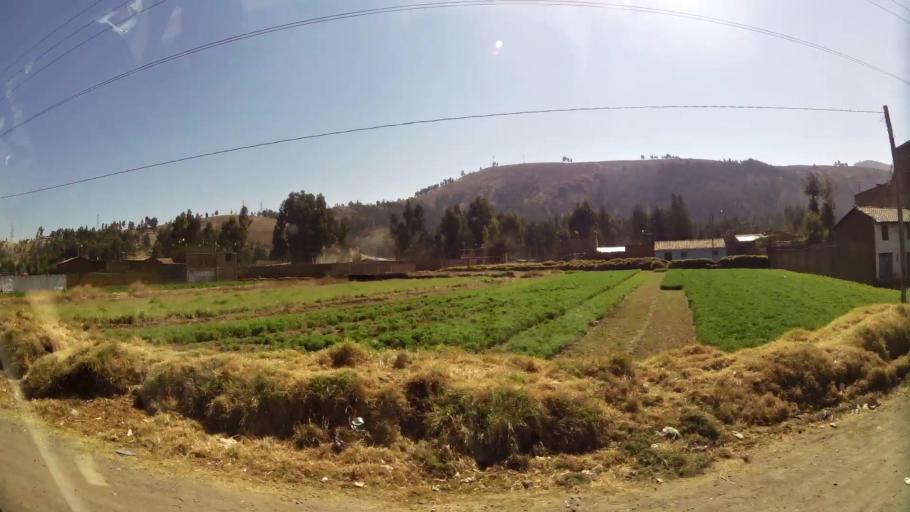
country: PE
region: Junin
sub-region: Provincia de Concepcion
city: Concepcion
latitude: -11.9396
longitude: -75.3046
